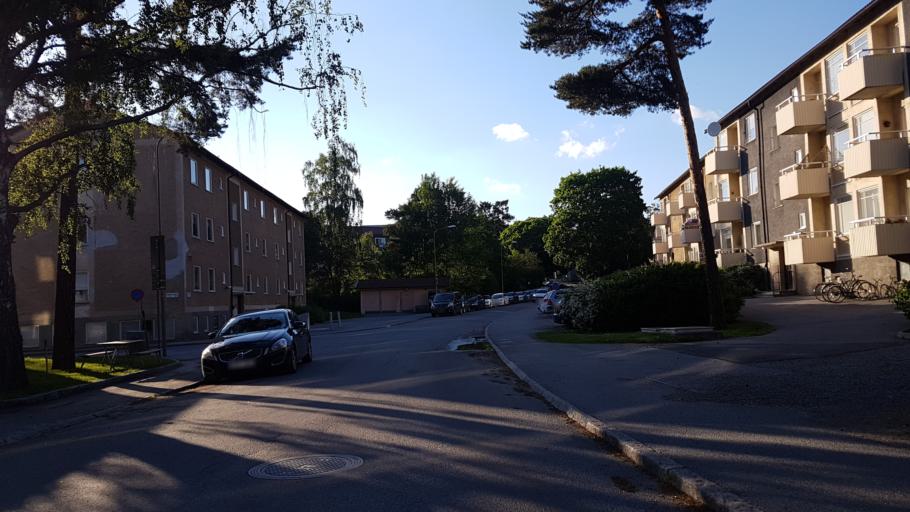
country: SE
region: Stockholm
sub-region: Nacka Kommun
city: Nacka
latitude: 59.2826
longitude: 18.1207
